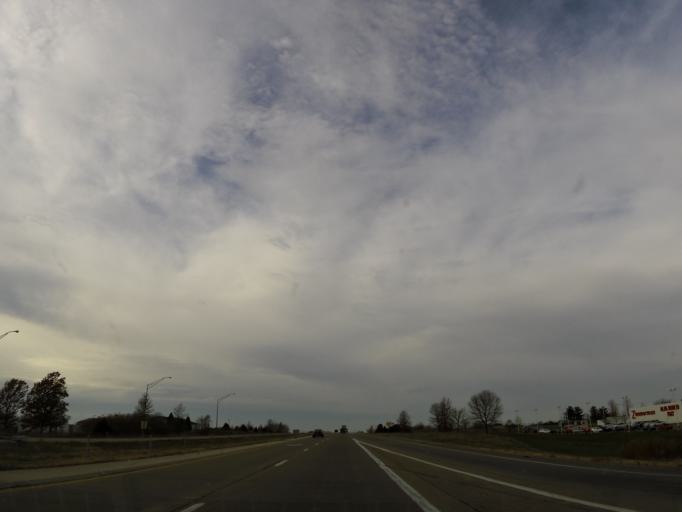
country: US
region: Iowa
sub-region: Scott County
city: Eldridge
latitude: 41.5971
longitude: -90.5749
